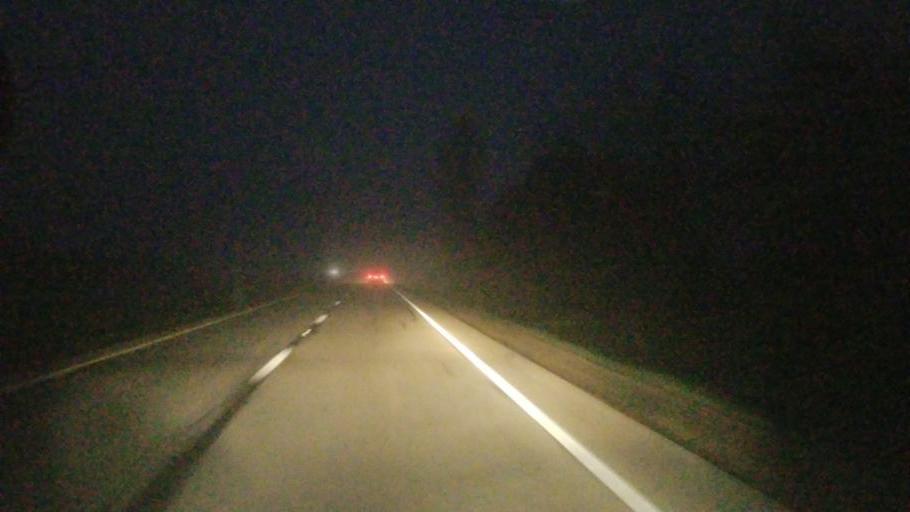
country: US
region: Ohio
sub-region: Ross County
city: Kingston
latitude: 39.4876
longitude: -82.9717
